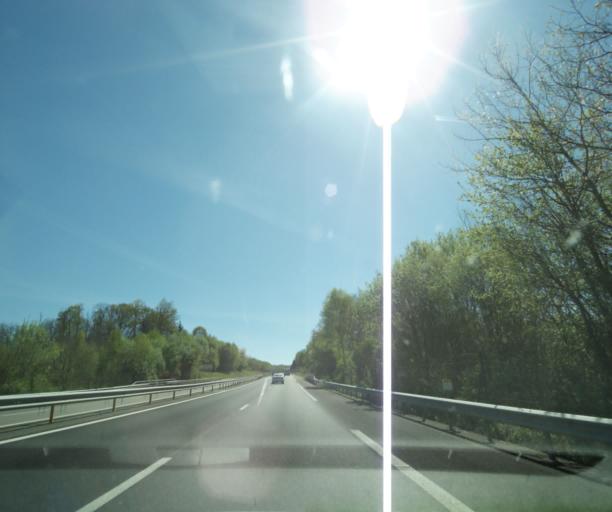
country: FR
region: Limousin
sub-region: Departement de la Correze
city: Uzerche
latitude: 45.3774
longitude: 1.5739
